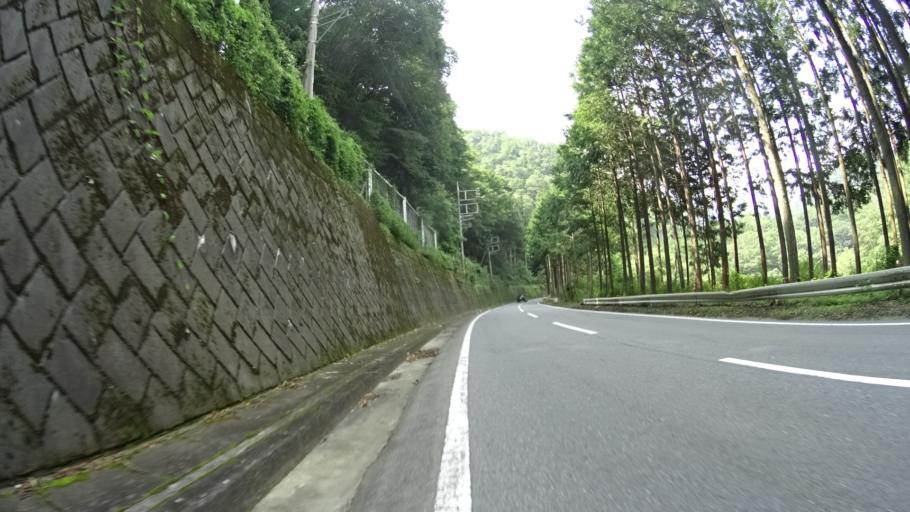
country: JP
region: Gunma
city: Tomioka
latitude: 36.0842
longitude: 138.8030
